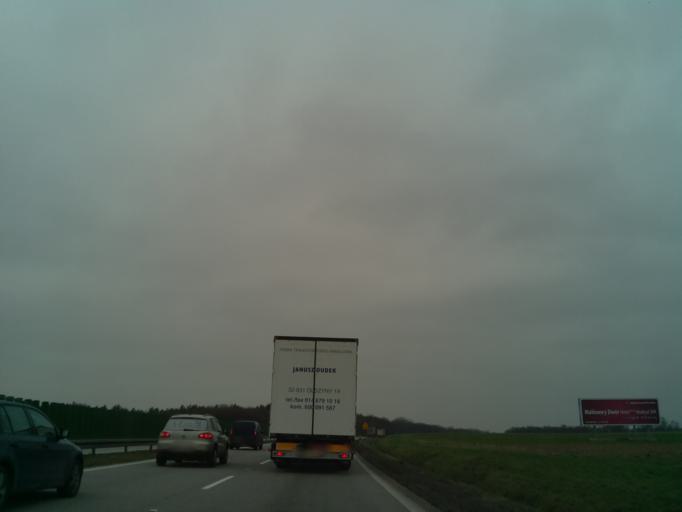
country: PL
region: Lower Silesian Voivodeship
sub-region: Powiat wroclawski
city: Katy Wroclawskie
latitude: 51.0196
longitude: 16.6956
